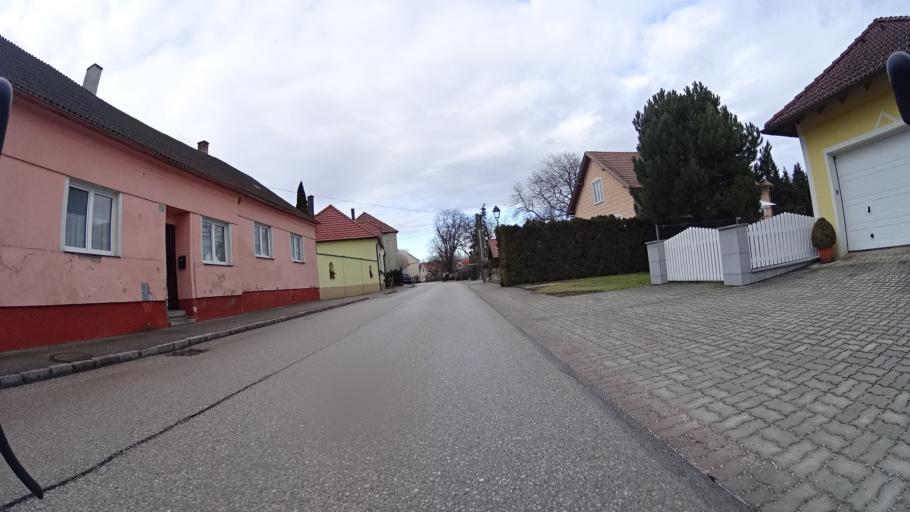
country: AT
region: Lower Austria
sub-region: Politischer Bezirk Tulln
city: Langenrohr
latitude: 48.3284
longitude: 15.9840
